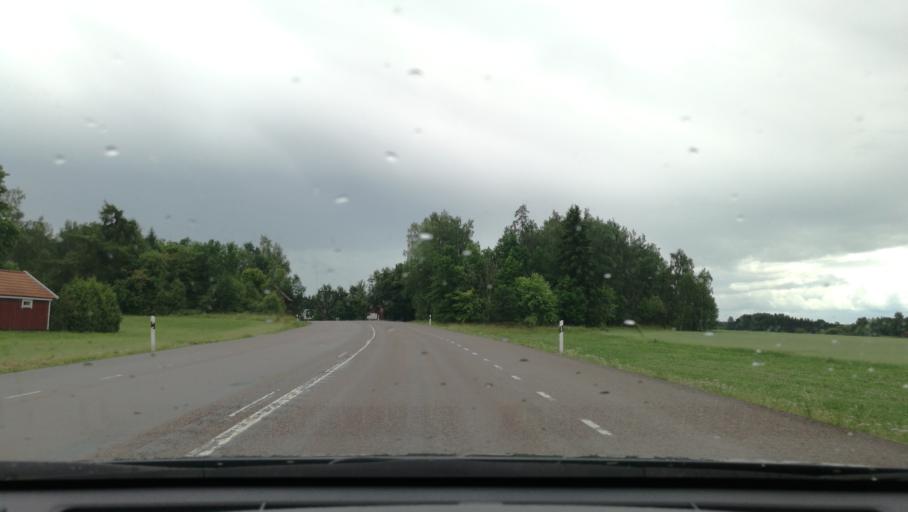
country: SE
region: Vaestmanland
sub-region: Kungsors Kommun
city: Kungsoer
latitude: 59.4438
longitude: 16.0452
